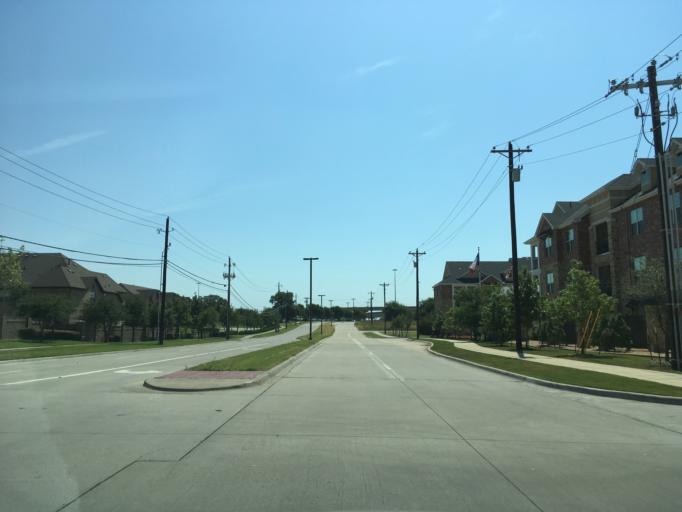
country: US
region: Texas
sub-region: Collin County
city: Fairview
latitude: 33.1590
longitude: -96.6513
